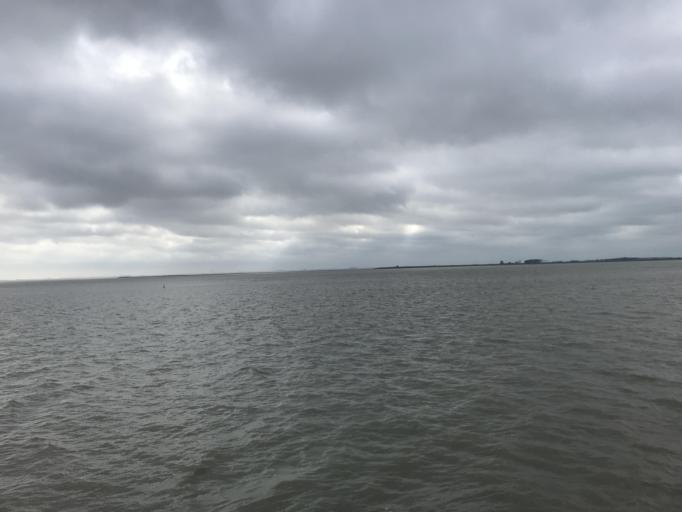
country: DE
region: Lower Saxony
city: Emden
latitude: 53.3254
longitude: 7.0681
